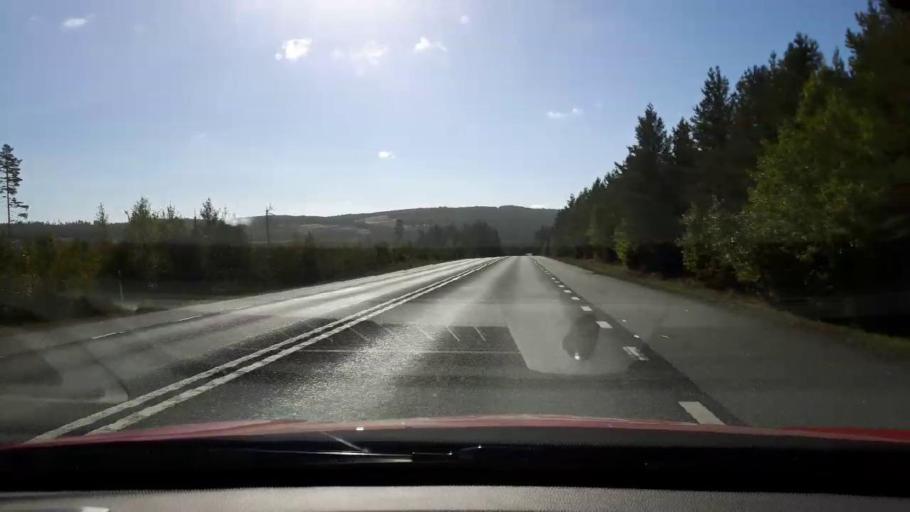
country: SE
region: Vaesternorrland
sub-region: Ange Kommun
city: Ange
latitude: 62.6796
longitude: 15.5916
